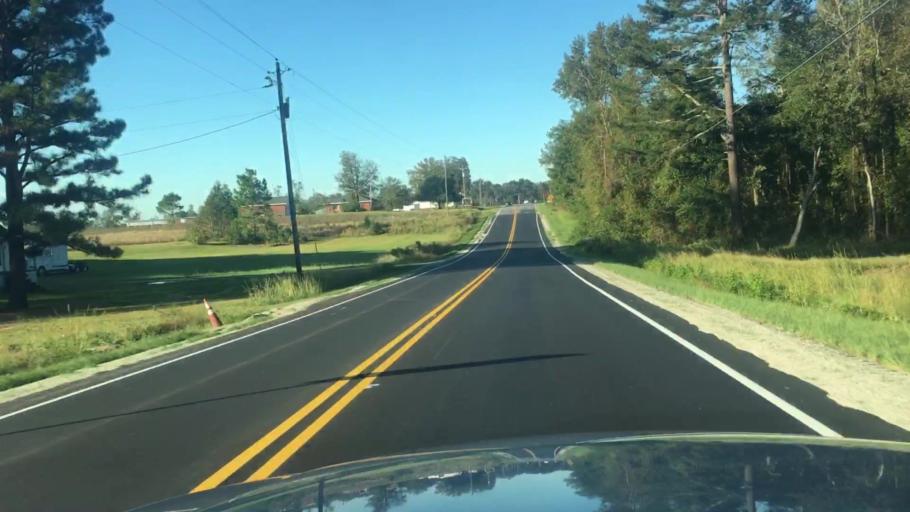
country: US
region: North Carolina
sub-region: Harnett County
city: Walkertown
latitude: 35.3158
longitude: -78.8809
